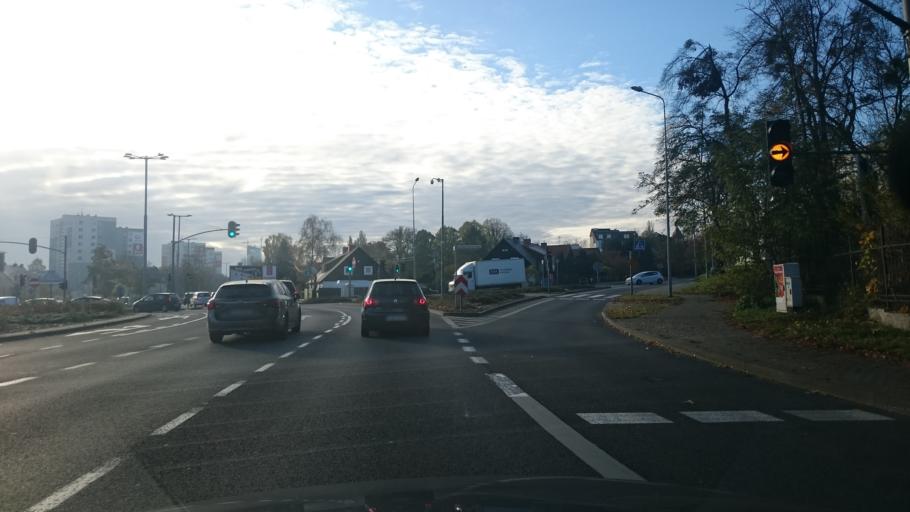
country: PL
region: Pomeranian Voivodeship
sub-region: Sopot
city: Sopot
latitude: 54.4238
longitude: 18.5636
